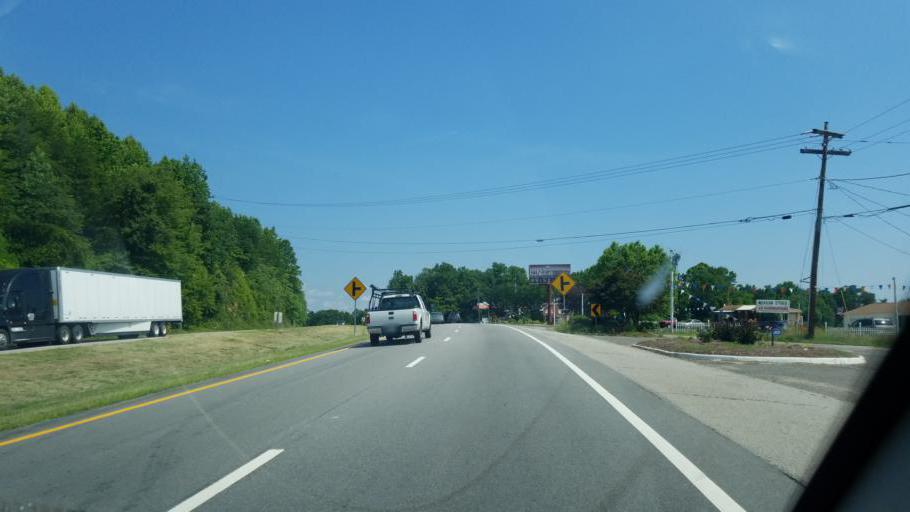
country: US
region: Virginia
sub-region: Pittsylvania County
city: Mount Hermon
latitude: 36.7432
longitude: -79.3781
